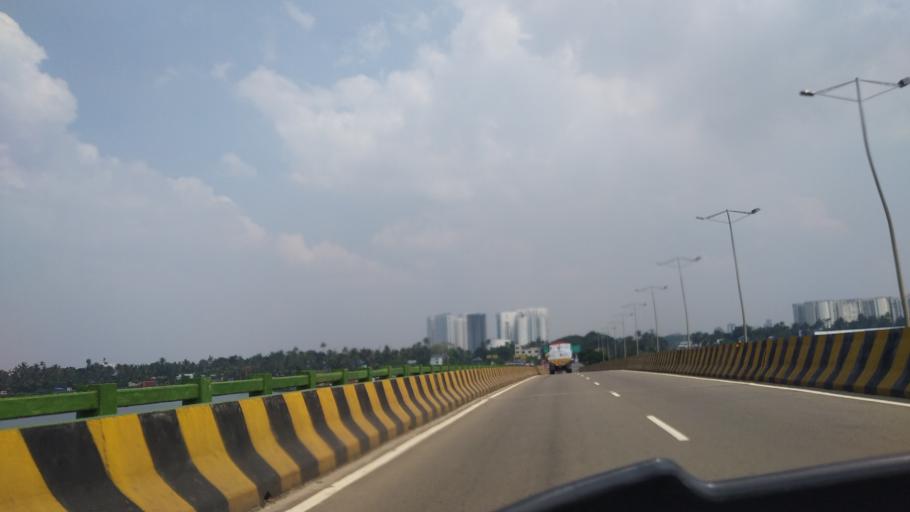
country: IN
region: Kerala
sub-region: Ernakulam
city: Cochin
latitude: 9.9900
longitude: 76.2616
